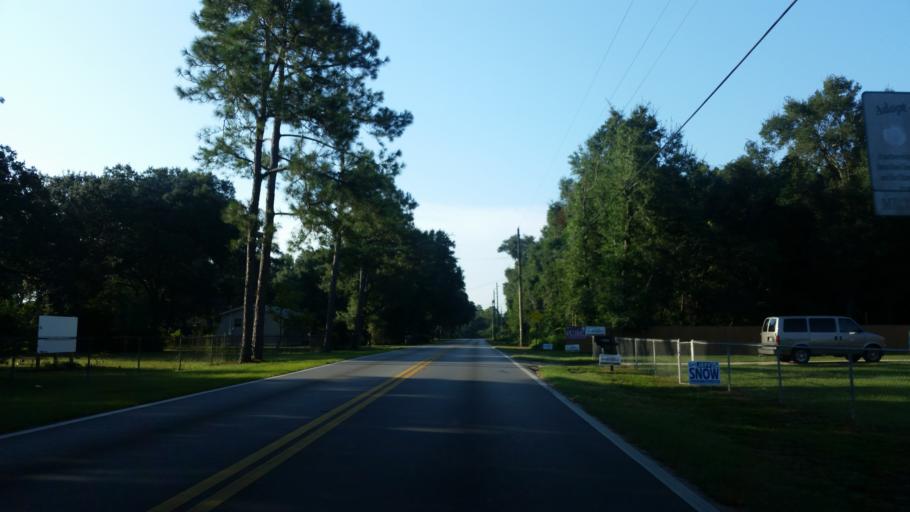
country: US
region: Florida
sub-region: Santa Rosa County
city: Milton
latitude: 30.6194
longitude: -87.0646
